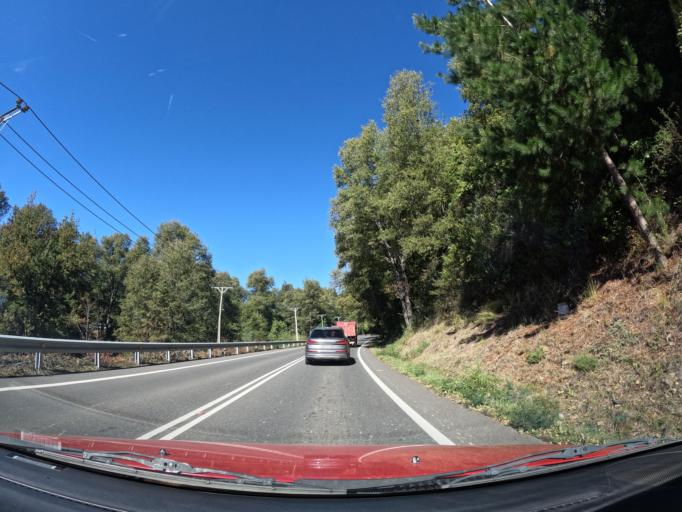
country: CL
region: Biobio
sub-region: Provincia de Nuble
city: Coihueco
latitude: -36.8047
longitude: -71.7435
